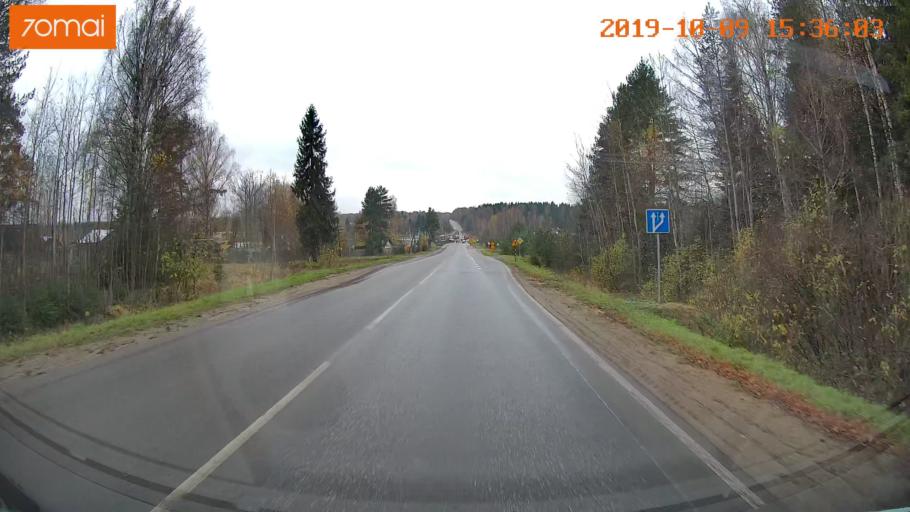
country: RU
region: Kostroma
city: Oktyabr'skiy
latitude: 57.9262
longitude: 41.2155
